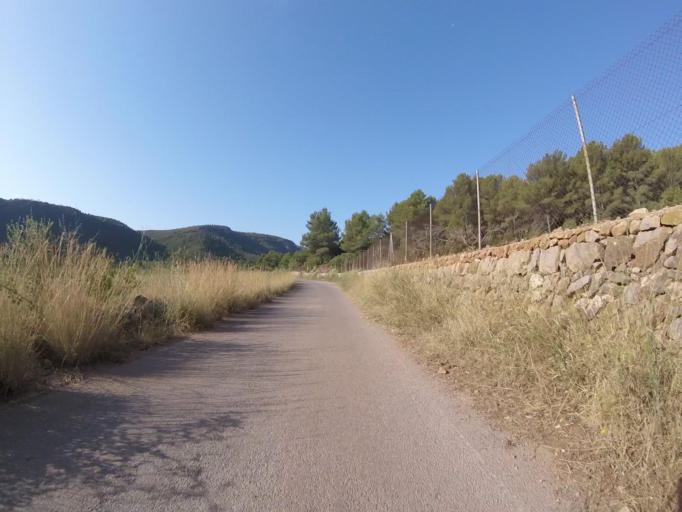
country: ES
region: Valencia
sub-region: Provincia de Castello
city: Benicassim
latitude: 40.1033
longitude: 0.0646
